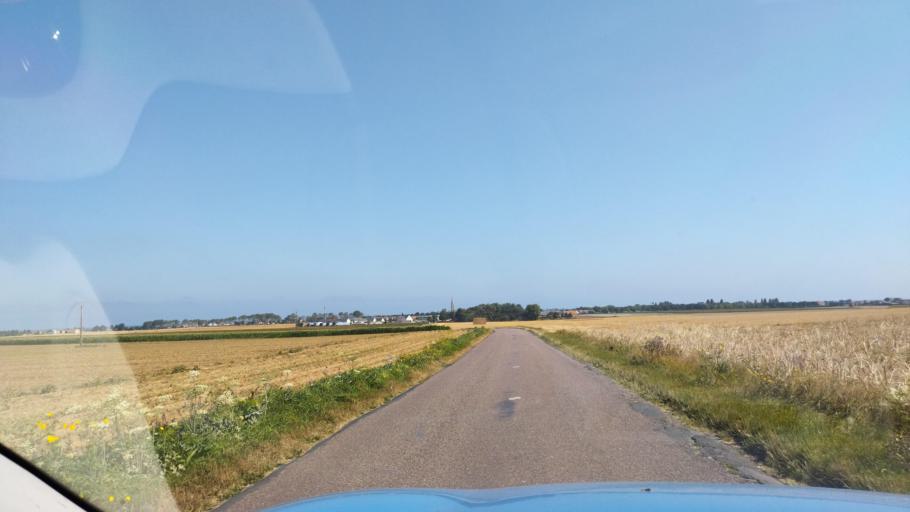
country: FR
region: Lower Normandy
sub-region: Departement du Calvados
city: Saint-Aubin-sur-Mer
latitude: 49.3148
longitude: -0.4033
